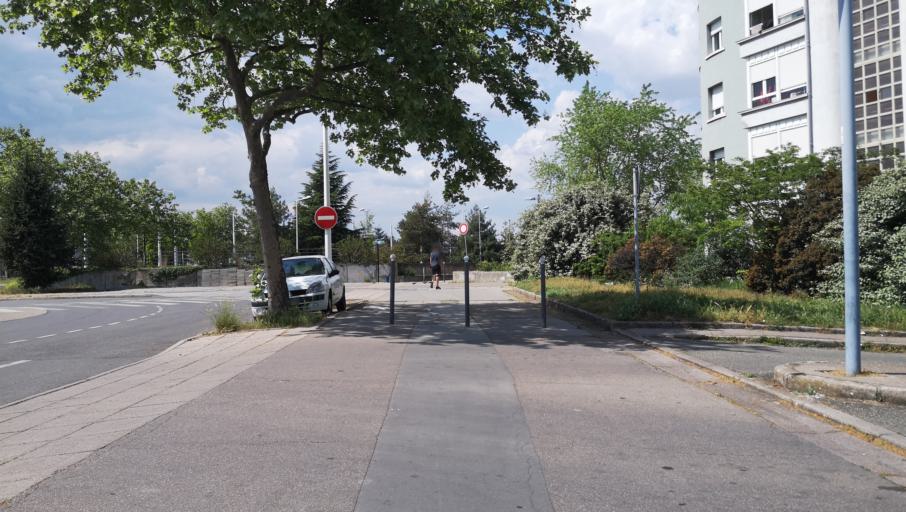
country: FR
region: Rhone-Alpes
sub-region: Departement du Rhone
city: Venissieux
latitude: 45.7202
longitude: 4.8880
